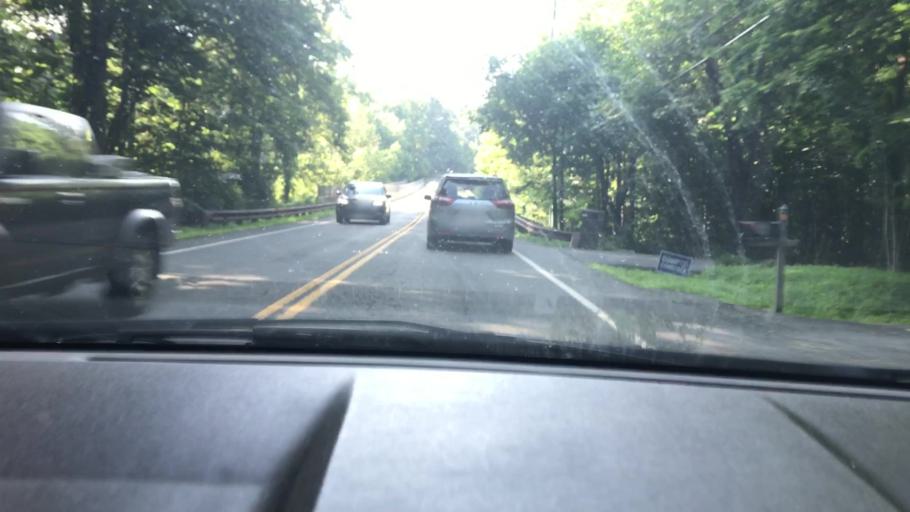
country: US
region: Virginia
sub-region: Fairfax County
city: Great Falls
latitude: 38.9744
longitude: -77.2541
